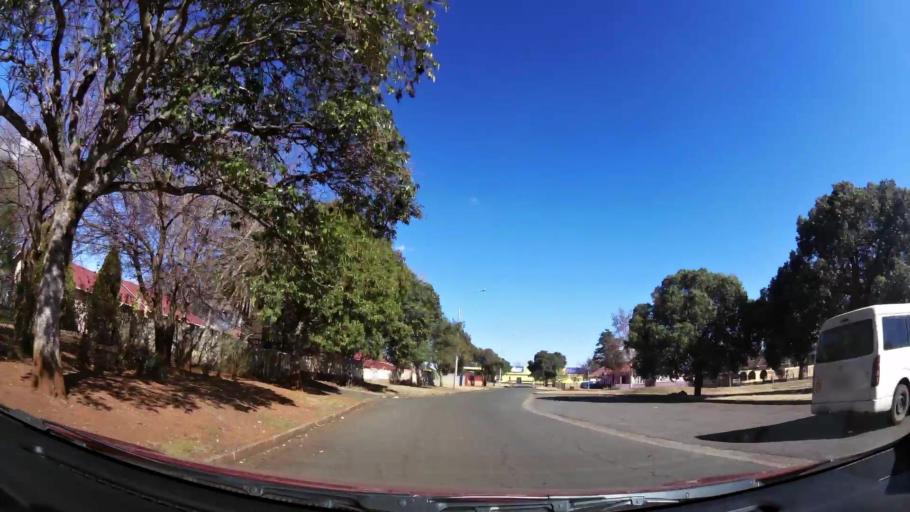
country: ZA
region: Gauteng
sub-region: West Rand District Municipality
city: Carletonville
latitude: -26.3636
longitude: 27.4012
